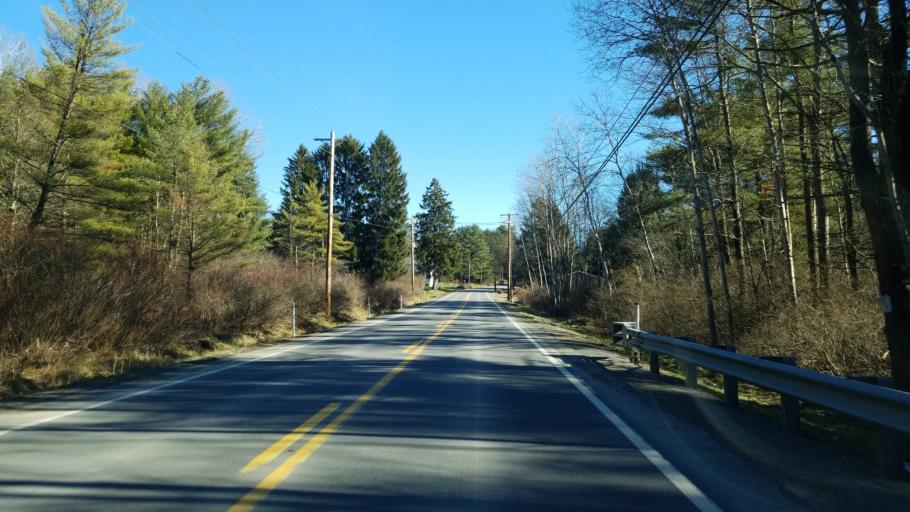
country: US
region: Pennsylvania
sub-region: Jefferson County
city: Falls Creek
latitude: 41.1770
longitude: -78.8441
